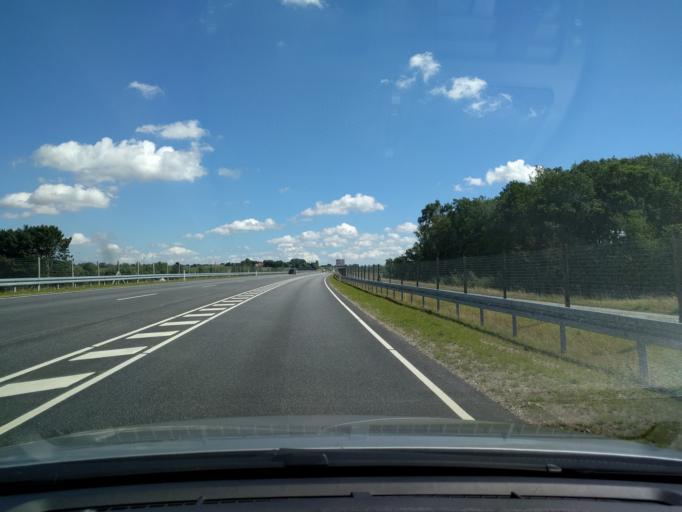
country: DK
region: Zealand
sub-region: Naestved Kommune
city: Naestved
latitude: 55.2625
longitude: 11.7451
